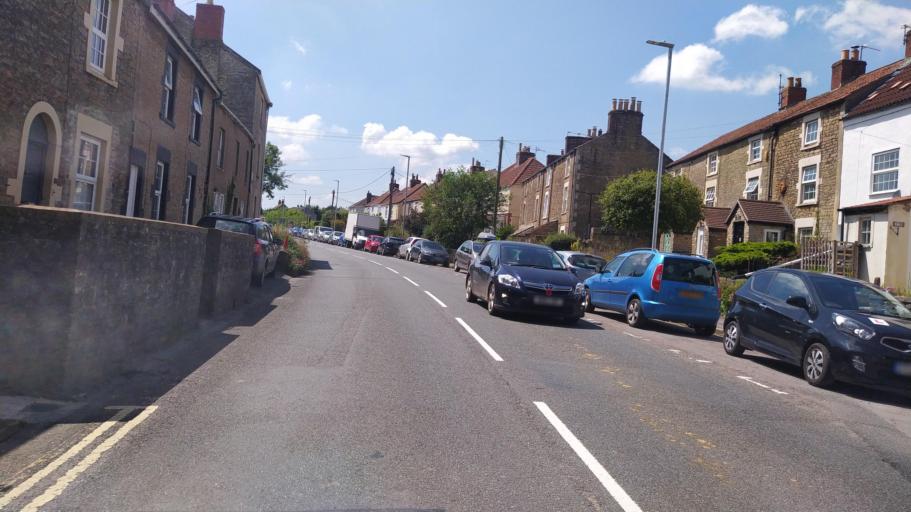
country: GB
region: England
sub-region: Somerset
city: Frome
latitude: 51.2224
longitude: -2.3306
